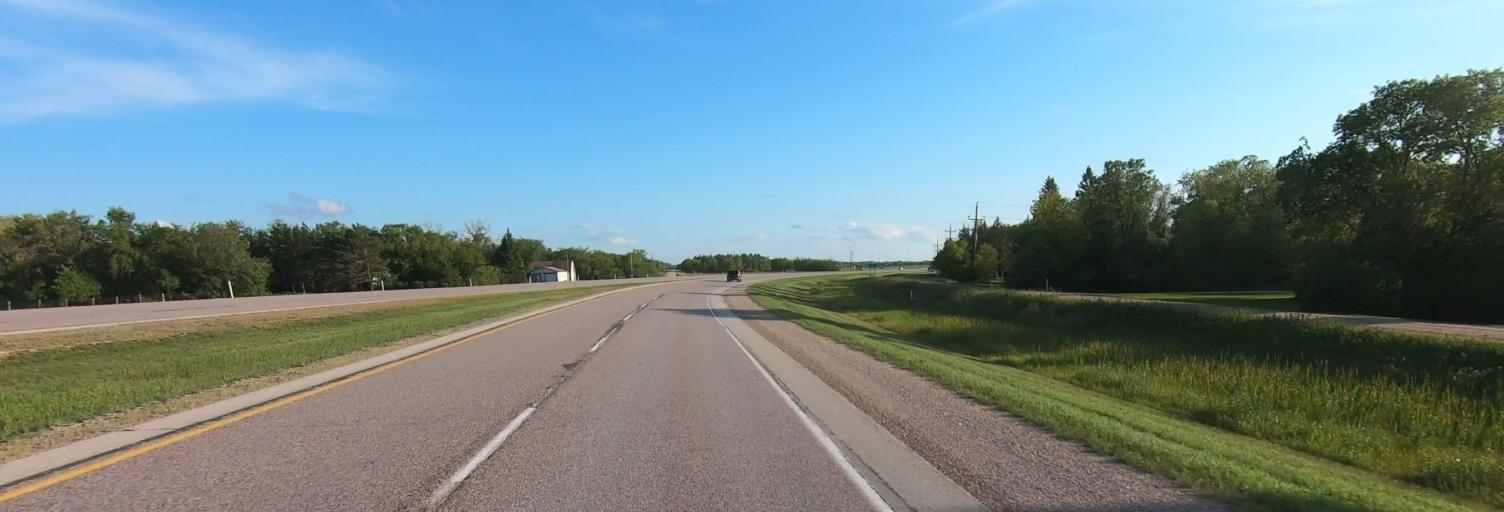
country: CA
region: Manitoba
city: Selkirk
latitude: 50.0899
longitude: -96.8643
